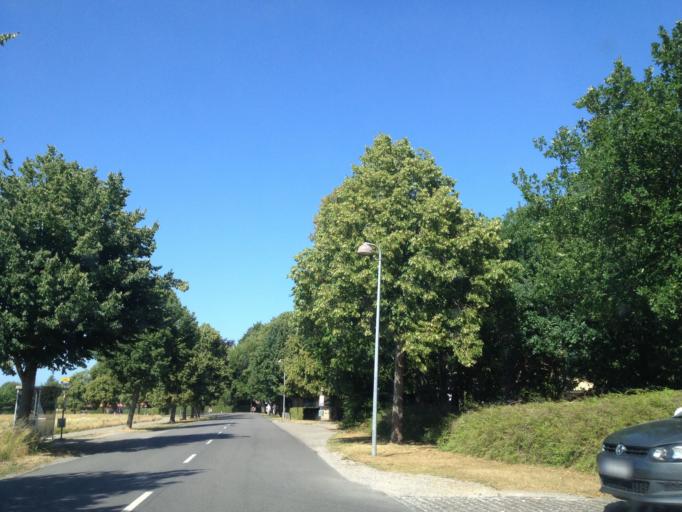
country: DK
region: Capital Region
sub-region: Fredensborg Kommune
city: Niva
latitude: 55.9263
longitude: 12.5102
